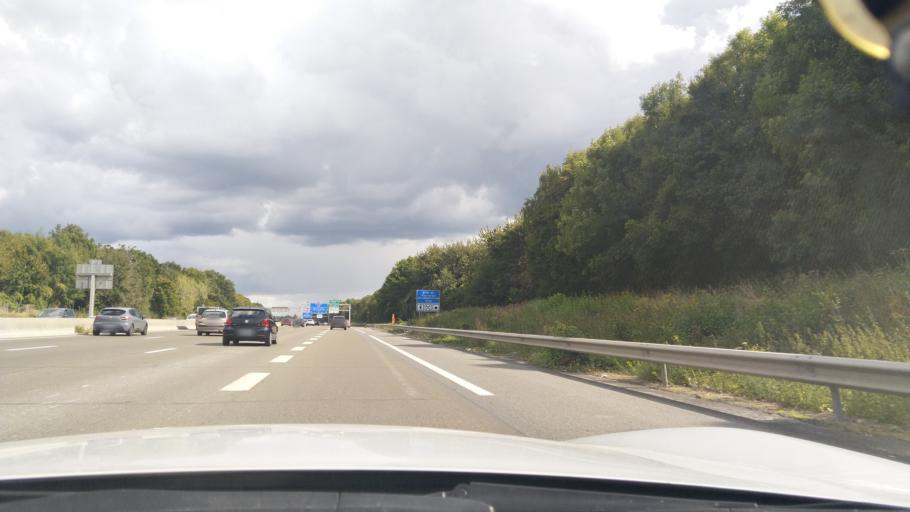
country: FR
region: Ile-de-France
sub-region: Departement de Seine-et-Marne
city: Champs-sur-Marne
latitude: 48.8303
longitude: 2.6019
